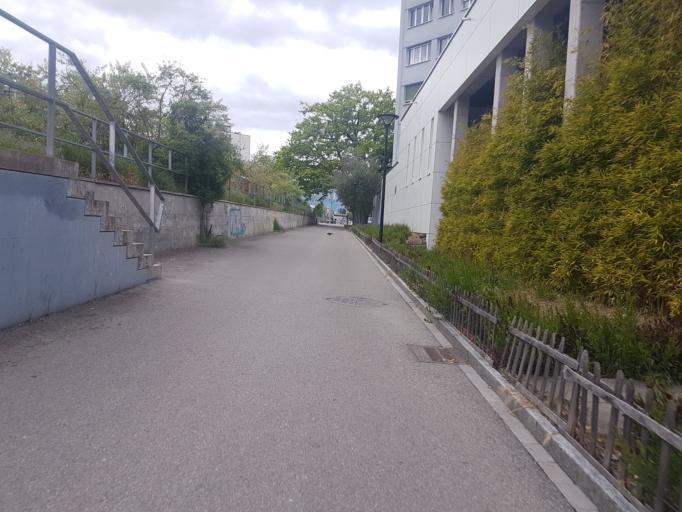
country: CH
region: Geneva
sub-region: Geneva
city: Lancy
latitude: 46.2068
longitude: 6.1232
